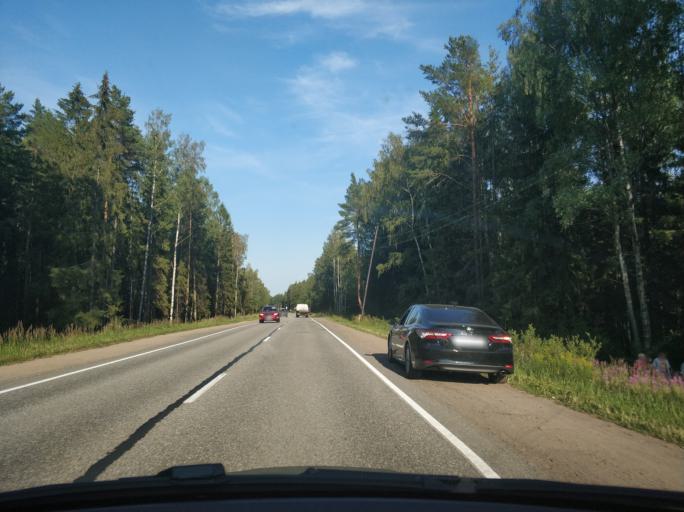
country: RU
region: Leningrad
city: Borisova Griva
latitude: 60.0918
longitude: 30.9964
